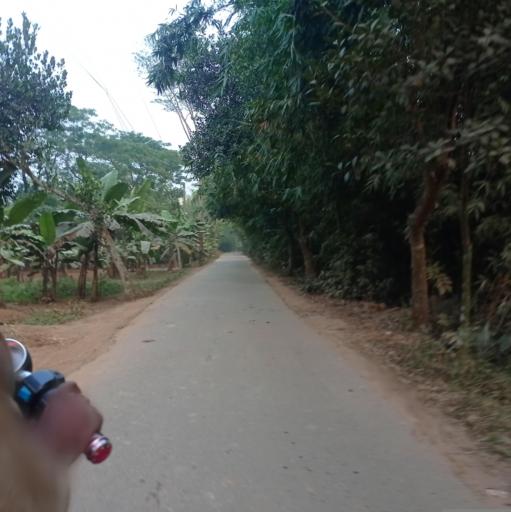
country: BD
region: Dhaka
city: Bajitpur
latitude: 24.1328
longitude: 90.8163
